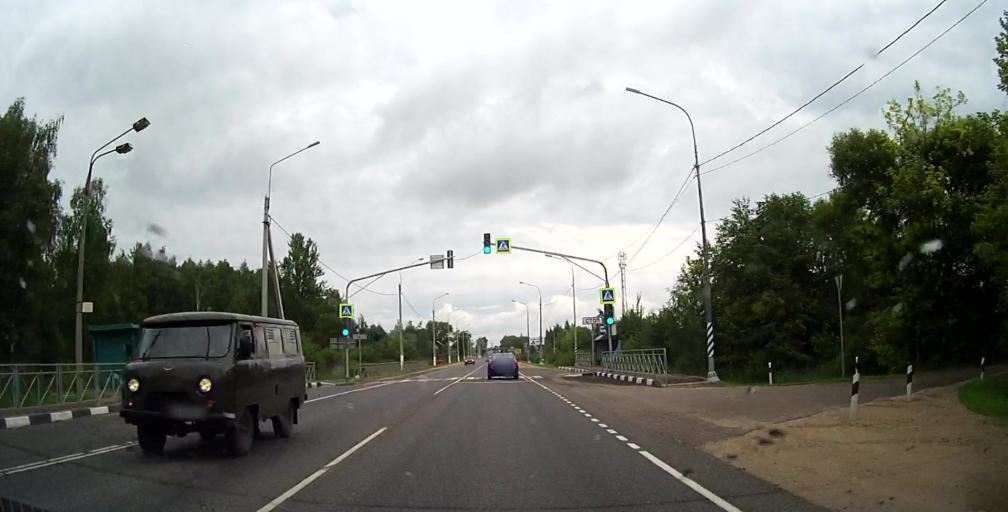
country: RU
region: Smolensk
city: Katyn'
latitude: 54.7798
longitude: 31.8075
